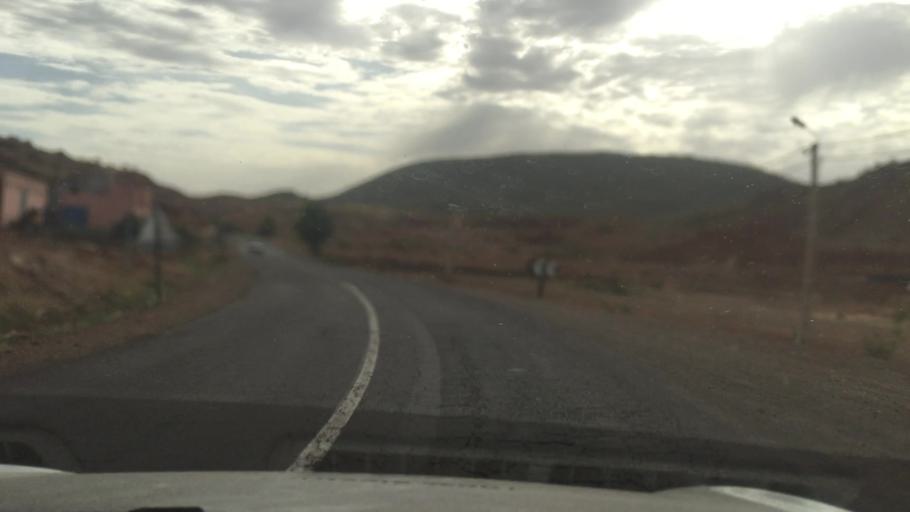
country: MA
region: Marrakech-Tensift-Al Haouz
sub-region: Al-Haouz
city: Touama
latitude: 31.5456
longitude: -7.5718
